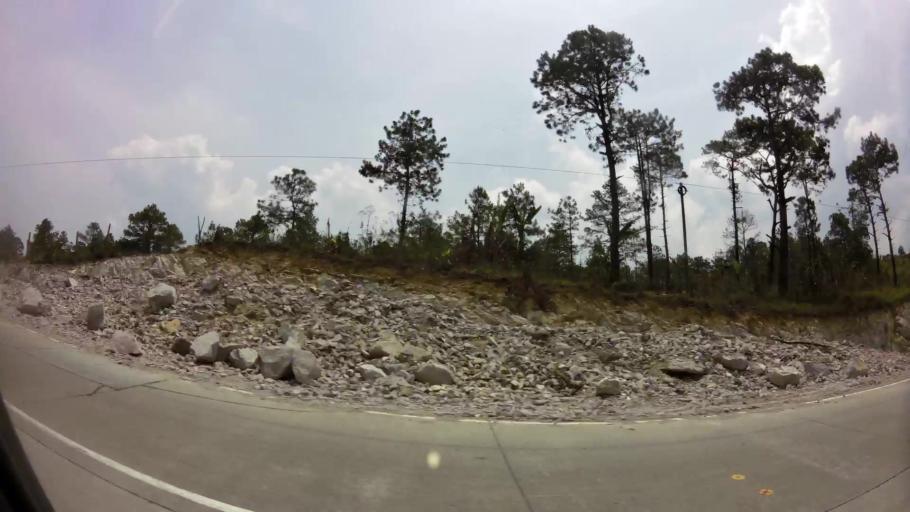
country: HN
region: Comayagua
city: El Socorro
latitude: 14.6457
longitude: -87.9267
